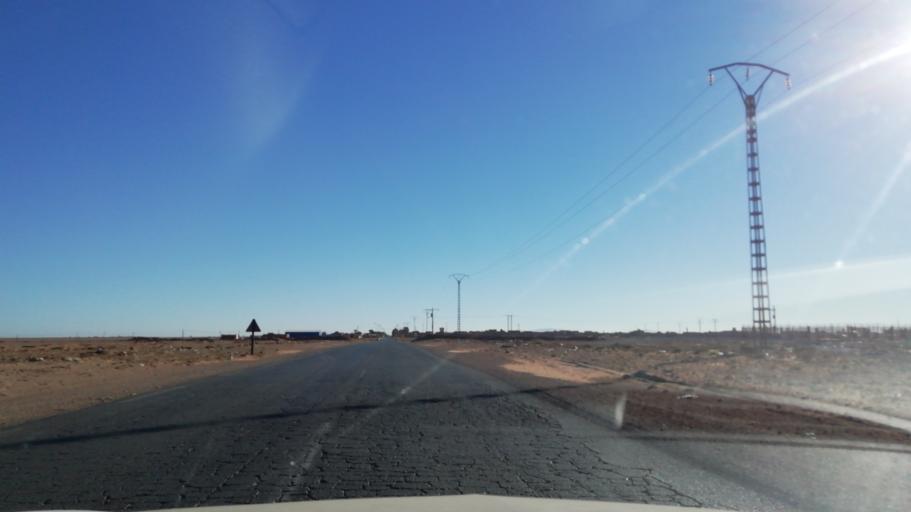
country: DZ
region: El Bayadh
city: El Bayadh
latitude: 33.8535
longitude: 0.6191
